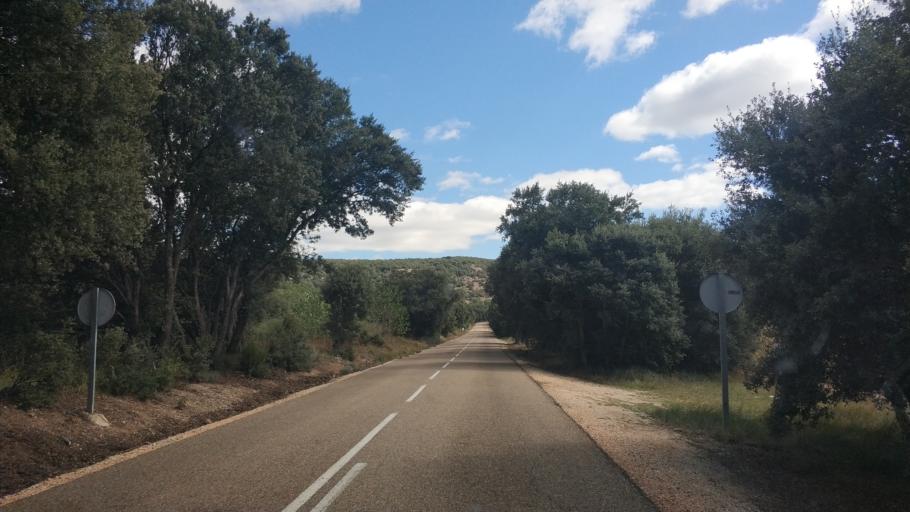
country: ES
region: Castille and Leon
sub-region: Provincia de Burgos
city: Retuerta
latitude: 42.0405
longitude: -3.4884
